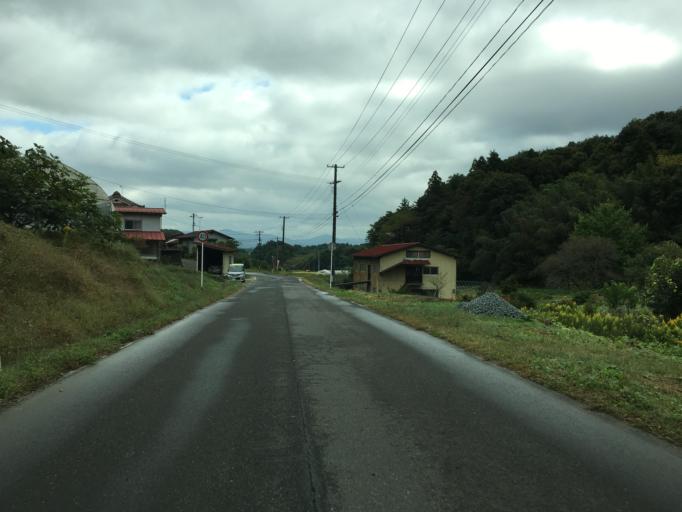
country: JP
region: Fukushima
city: Nihommatsu
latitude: 37.6287
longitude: 140.4414
